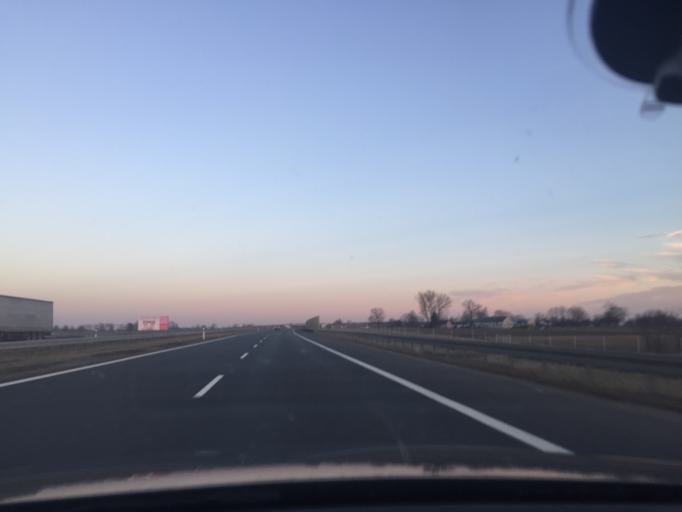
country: PL
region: Lodz Voivodeship
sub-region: Powiat poddebicki
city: Dalikow
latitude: 51.9646
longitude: 19.1130
